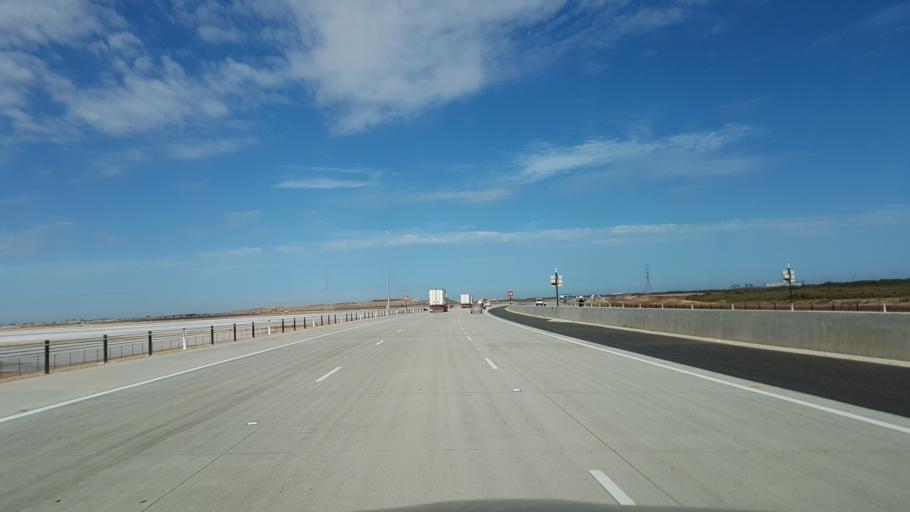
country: AU
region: South Australia
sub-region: Port Adelaide Enfield
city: Enfield
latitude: -34.8051
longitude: 138.5736
